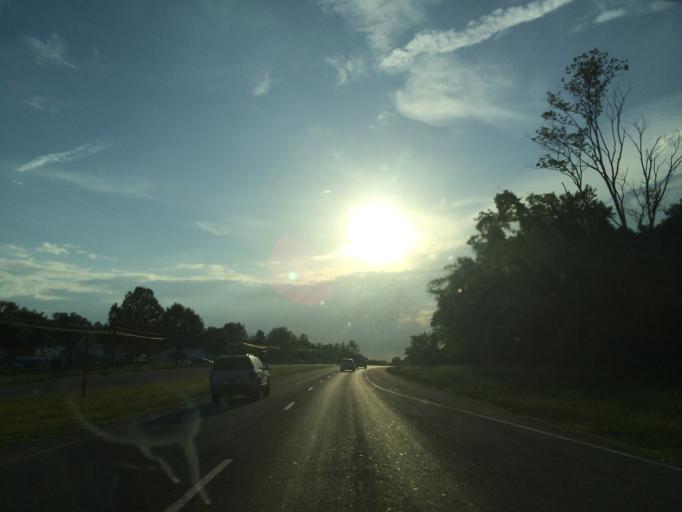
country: US
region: Maryland
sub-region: Howard County
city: Columbia
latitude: 39.2805
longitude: -76.8687
